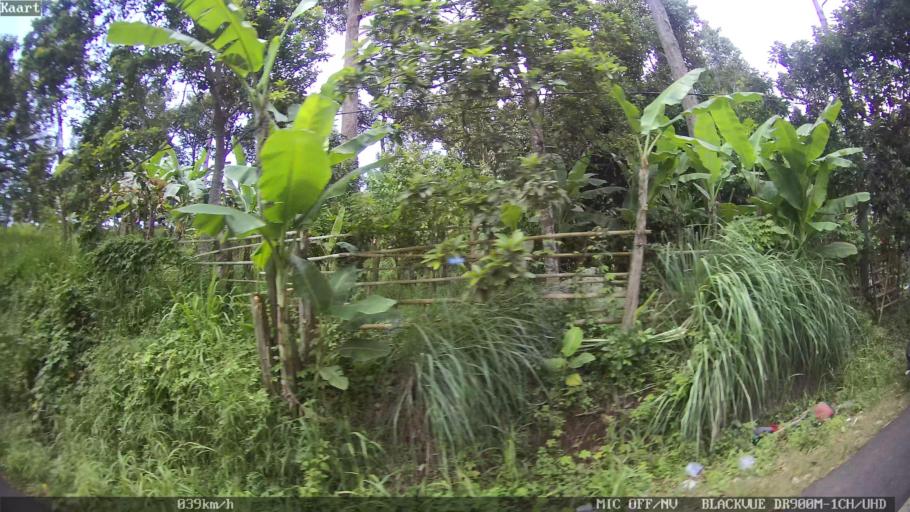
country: ID
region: Lampung
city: Bandarlampung
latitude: -5.4156
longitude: 105.2301
